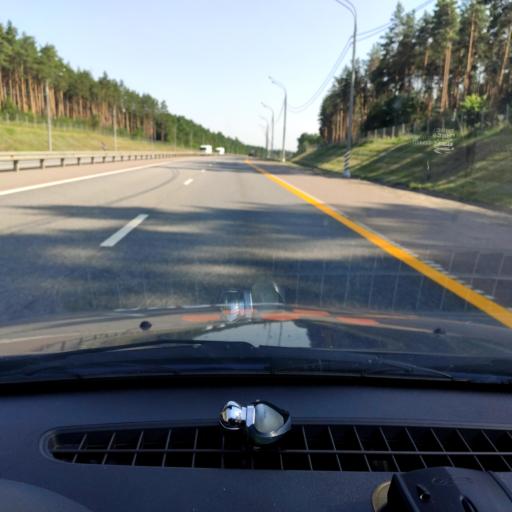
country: RU
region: Lipetsk
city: Khlevnoye
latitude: 52.3067
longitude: 39.0495
